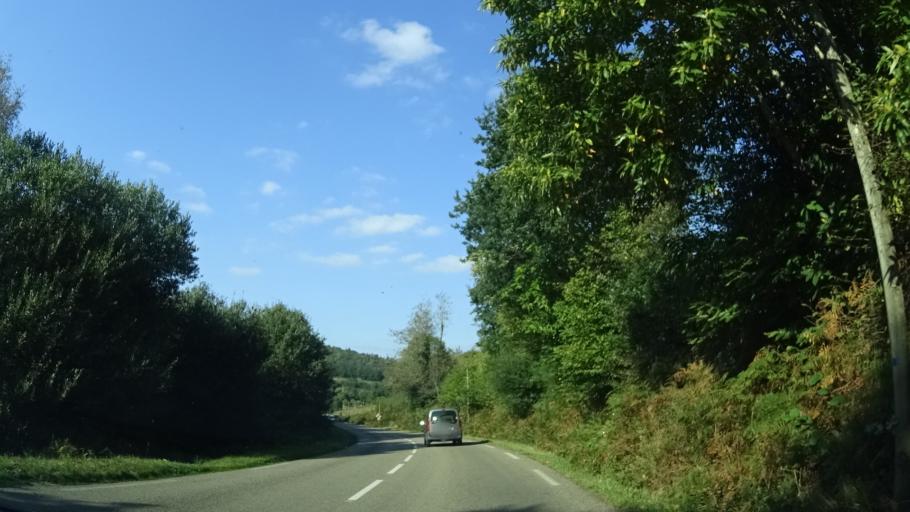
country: FR
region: Brittany
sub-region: Departement du Finistere
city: Chateaulin
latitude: 48.1877
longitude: -4.1093
